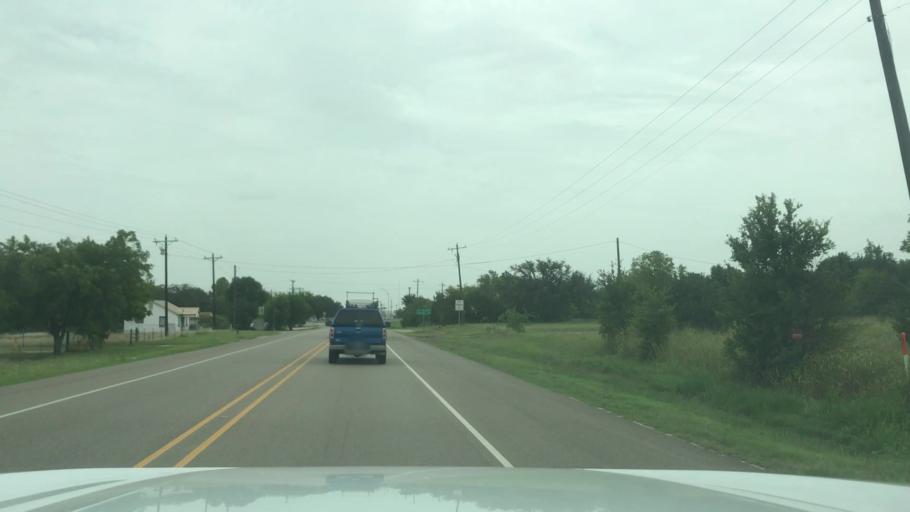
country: US
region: Texas
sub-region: Bosque County
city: Meridian
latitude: 31.9176
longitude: -97.6693
